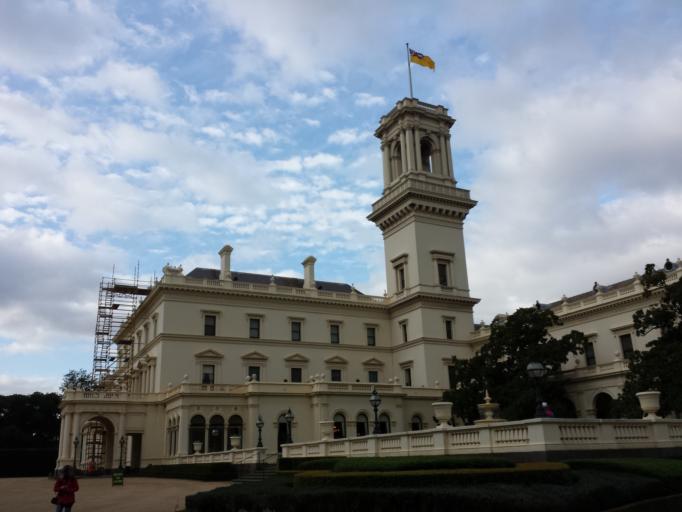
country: AU
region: Victoria
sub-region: Port Phillip
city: South Melbourne
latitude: -37.8279
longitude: 144.9763
